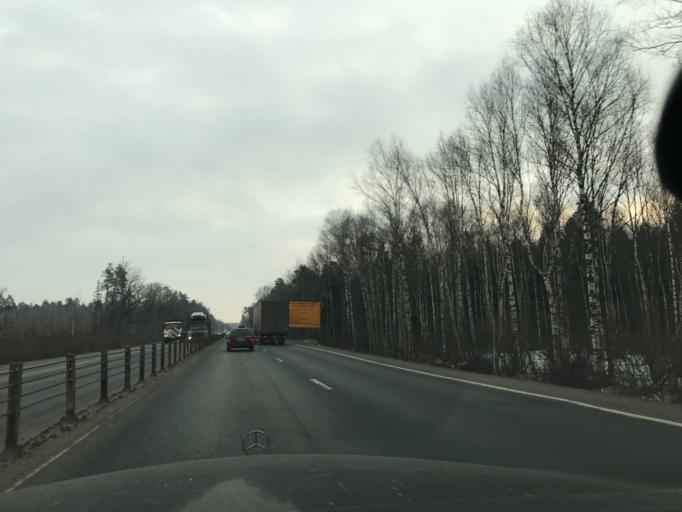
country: RU
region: Moskovskaya
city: Malaya Dubna
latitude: 55.8952
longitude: 39.0397
